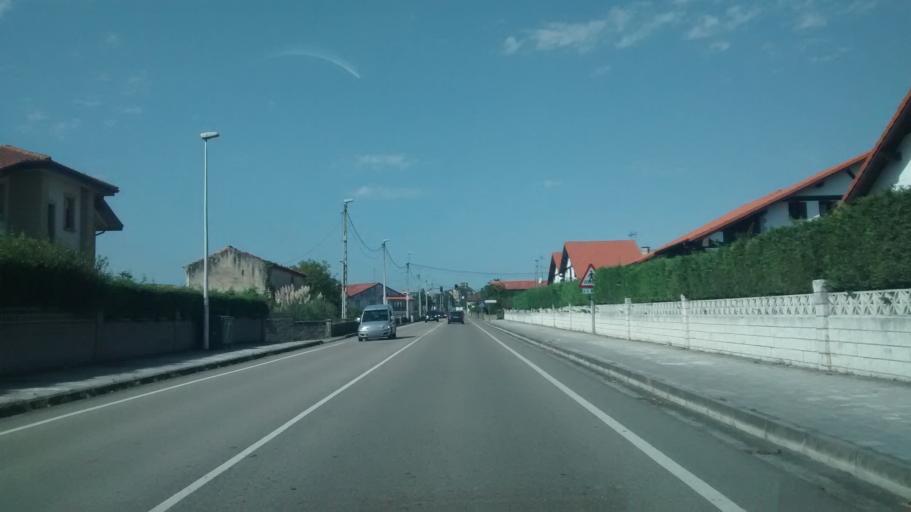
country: ES
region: Cantabria
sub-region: Provincia de Cantabria
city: Arnuero
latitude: 43.4603
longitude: -3.5425
